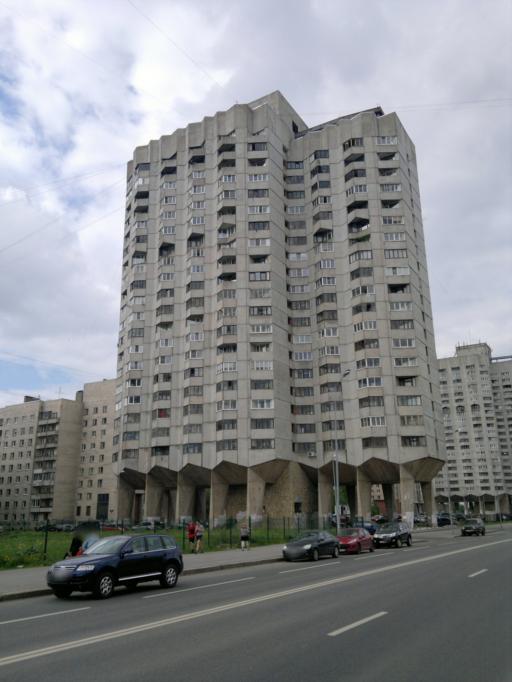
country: RU
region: St.-Petersburg
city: Vasyl'evsky Ostrov
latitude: 59.9482
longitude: 30.2245
